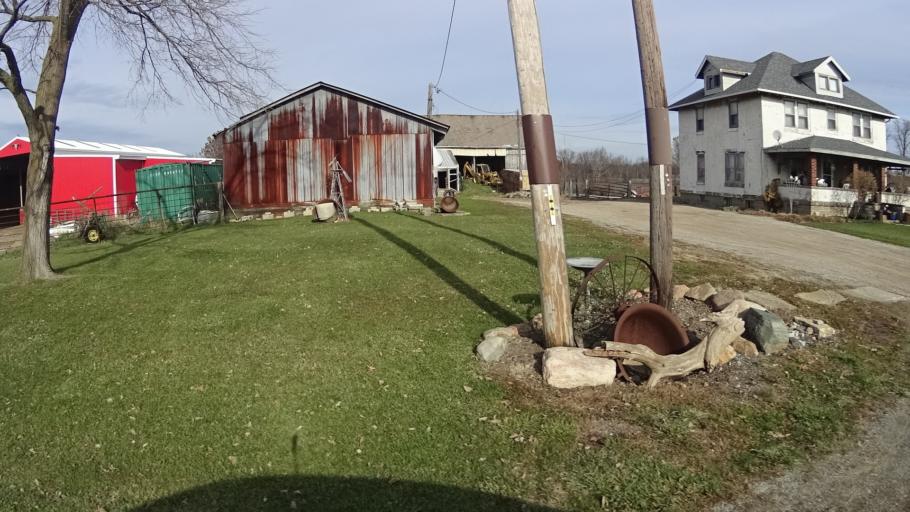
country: US
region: Ohio
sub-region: Lorain County
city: Grafton
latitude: 41.2226
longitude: -82.0063
